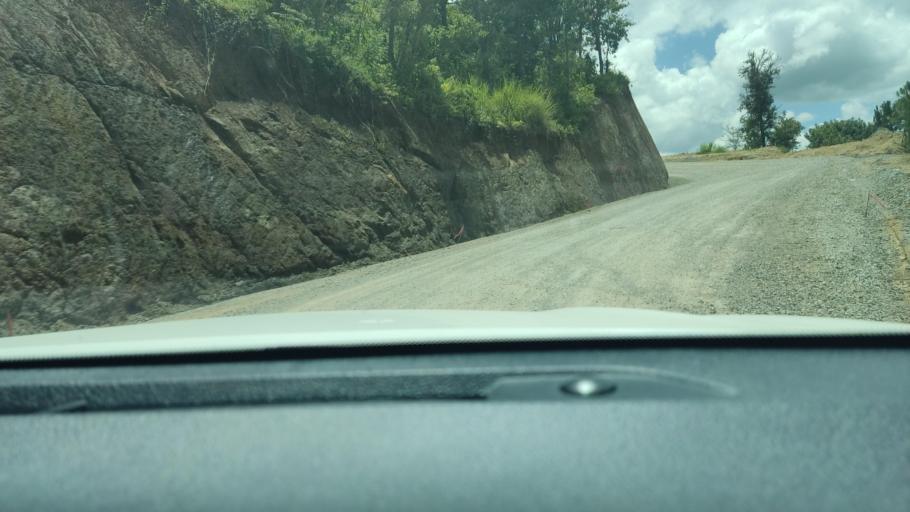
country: GT
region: Chimaltenango
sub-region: Municipio de San Juan Comalapa
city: Comalapa
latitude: 14.7882
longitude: -90.8620
